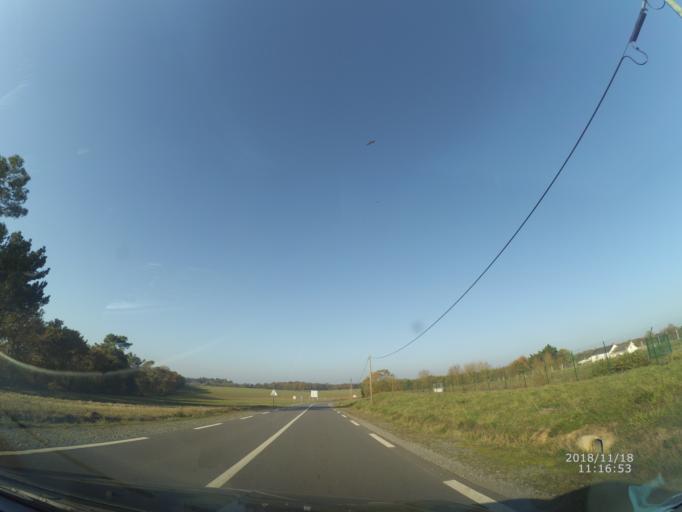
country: FR
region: Pays de la Loire
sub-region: Departement de la Loire-Atlantique
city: Saint-Pere-en-Retz
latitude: 47.2159
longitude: -2.0559
